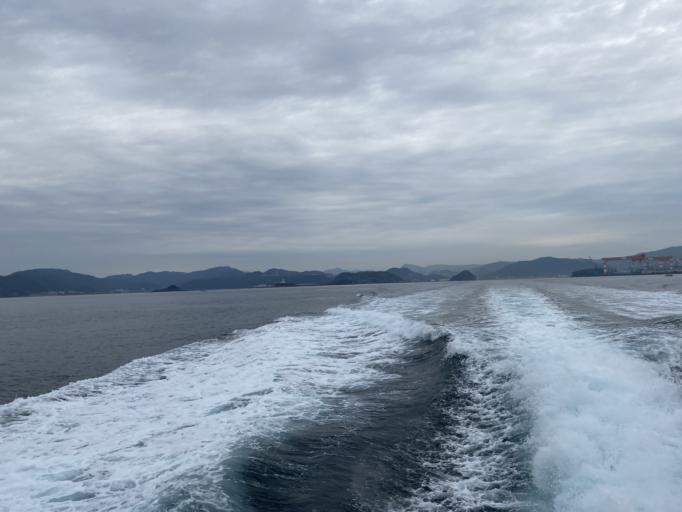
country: JP
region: Nagasaki
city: Nagasaki-shi
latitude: 32.7037
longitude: 129.7871
